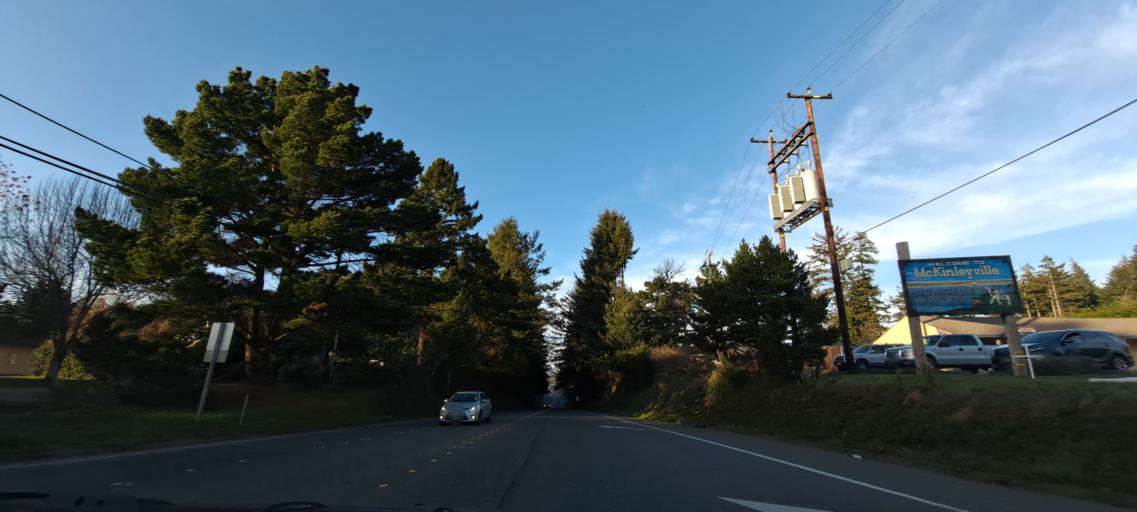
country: US
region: California
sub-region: Humboldt County
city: McKinleyville
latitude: 40.9272
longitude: -124.1008
